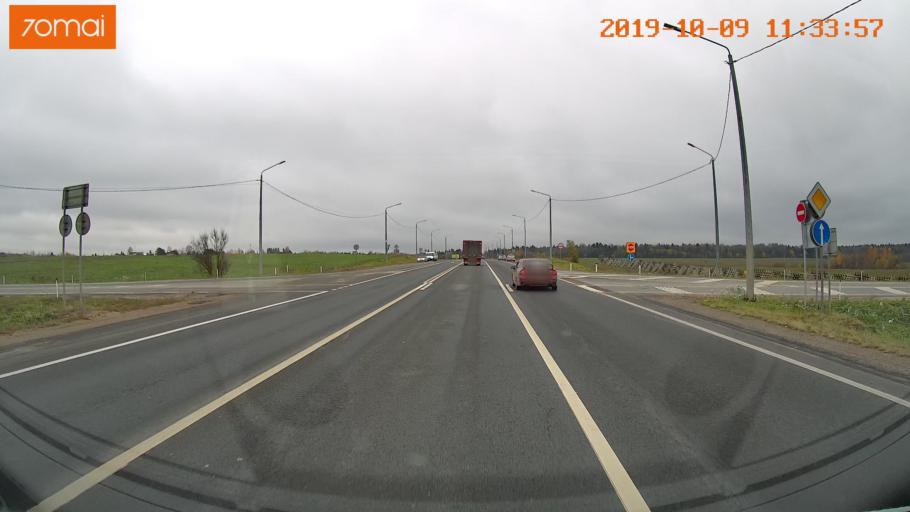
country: RU
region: Vologda
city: Gryazovets
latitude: 59.0206
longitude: 40.1160
